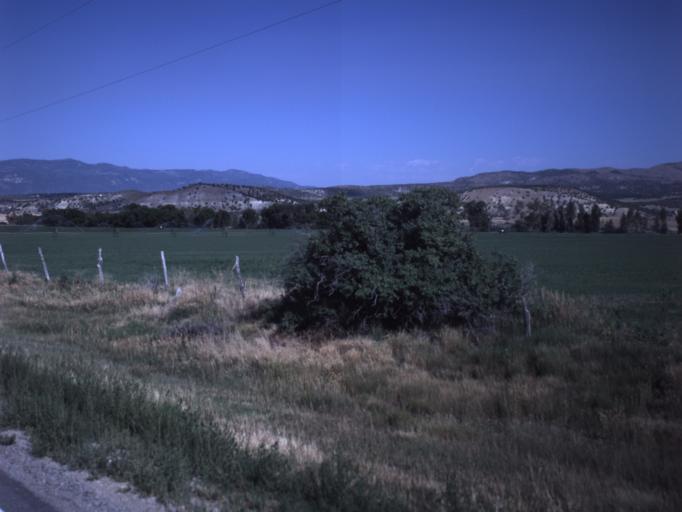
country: US
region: Utah
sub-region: Sanpete County
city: Mount Pleasant
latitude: 39.5468
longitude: -111.4853
